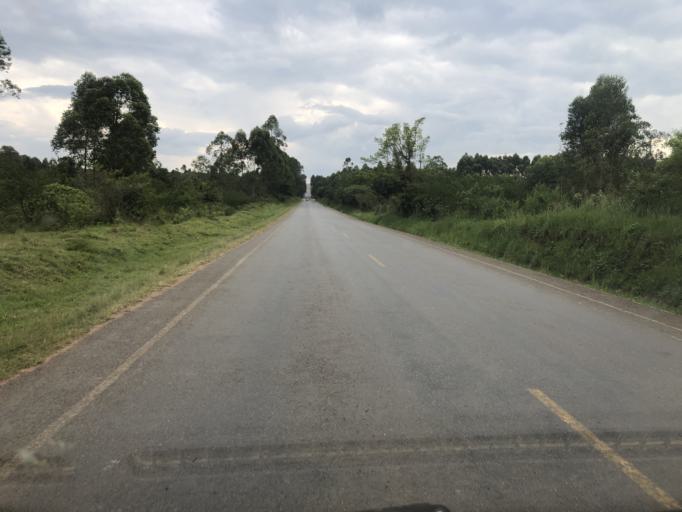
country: UG
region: Western Region
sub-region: Sheema District
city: Kibingo
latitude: -0.5791
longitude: 30.4169
